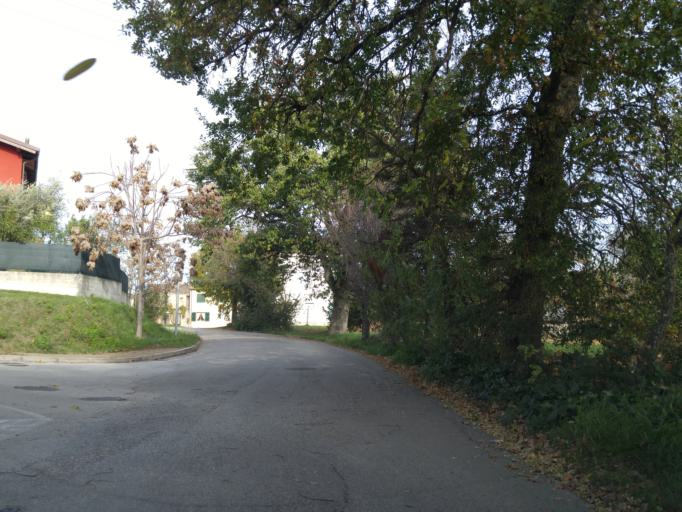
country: IT
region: The Marches
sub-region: Provincia di Pesaro e Urbino
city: Saltara
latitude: 43.7502
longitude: 12.9034
